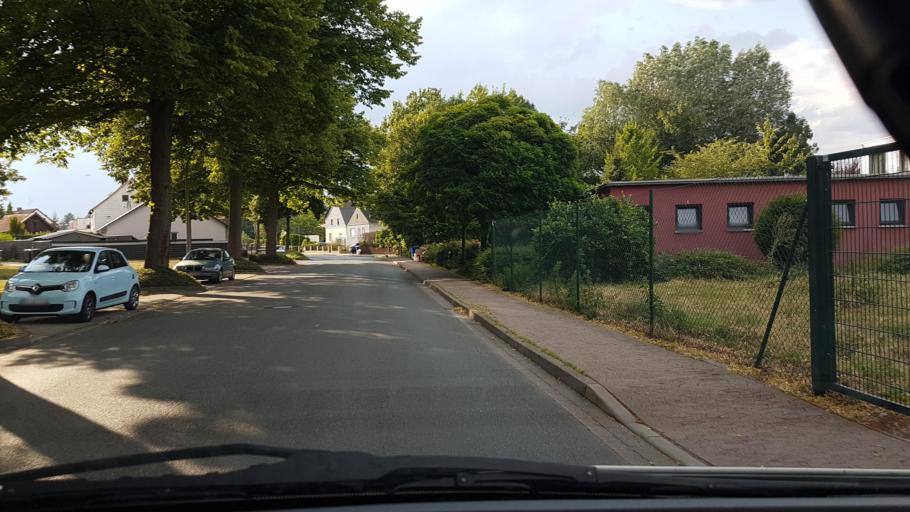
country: DE
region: Lower Saxony
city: Konigslutter am Elm
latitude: 52.2525
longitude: 10.8245
